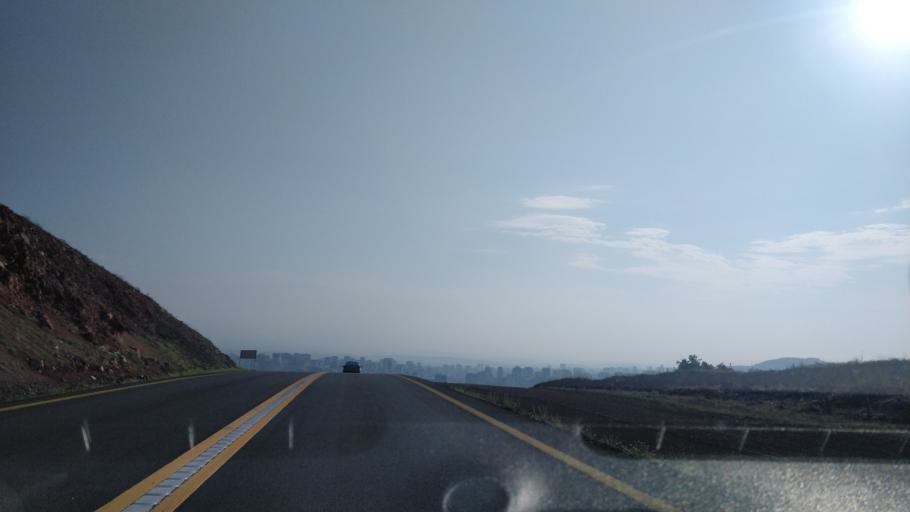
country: TR
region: Ankara
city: Etimesgut
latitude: 39.8749
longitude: 32.5973
